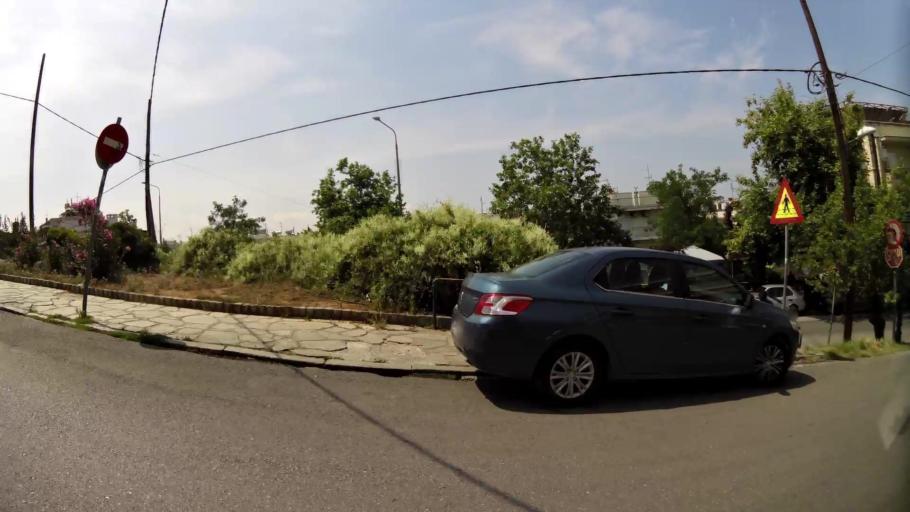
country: GR
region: Central Macedonia
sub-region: Nomos Thessalonikis
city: Agios Pavlos
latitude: 40.6326
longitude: 22.9632
